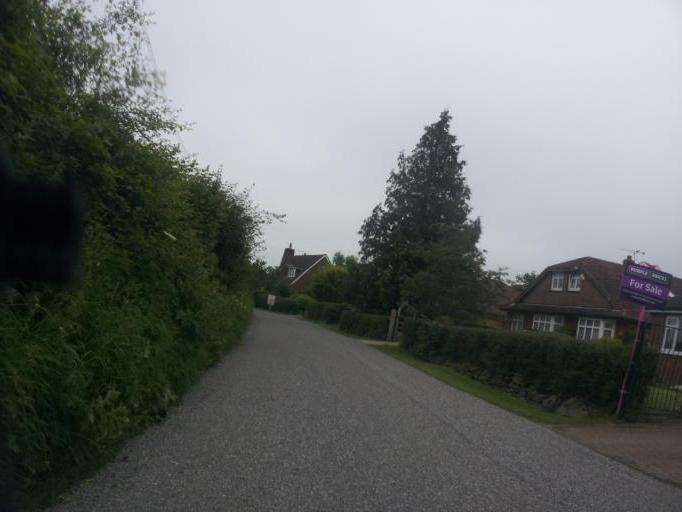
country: GB
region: England
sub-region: Kent
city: Maidstone
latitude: 51.2471
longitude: 0.5717
